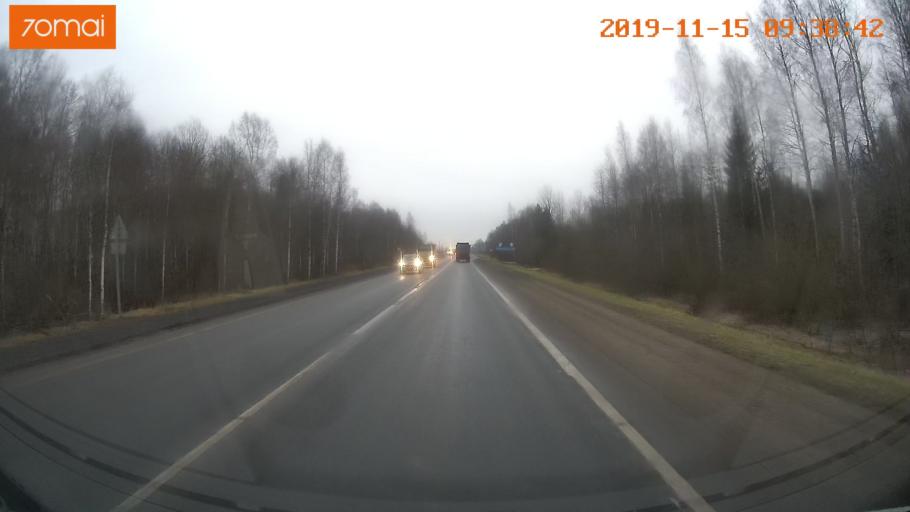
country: RU
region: Vologda
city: Sheksna
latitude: 59.2295
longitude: 38.4606
